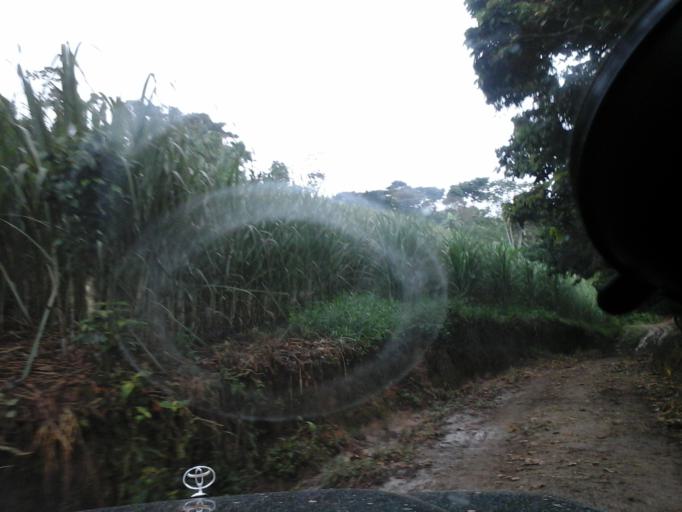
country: CO
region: Cesar
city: Agustin Codazzi
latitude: 9.9621
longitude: -73.0610
